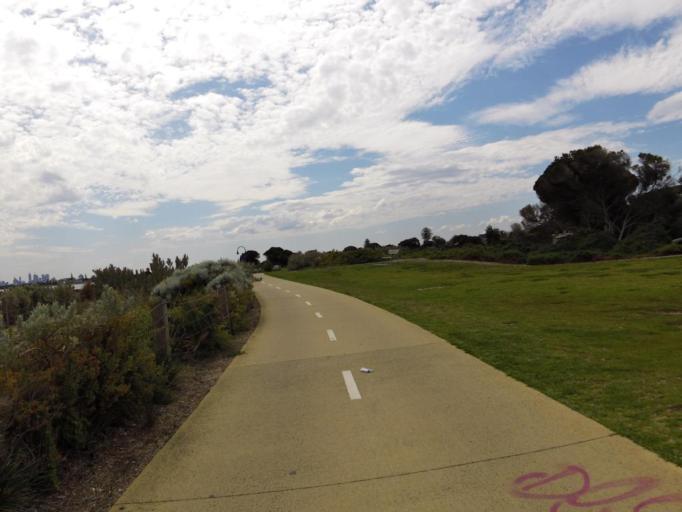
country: AU
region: Victoria
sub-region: Port Phillip
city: Elwood
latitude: -37.9005
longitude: 144.9840
